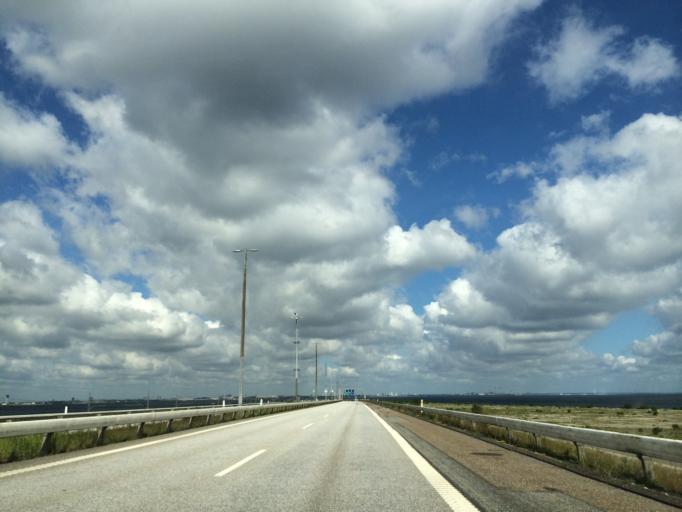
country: DK
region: Capital Region
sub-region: Dragor Kommune
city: Dragor
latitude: 55.6045
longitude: 12.7423
